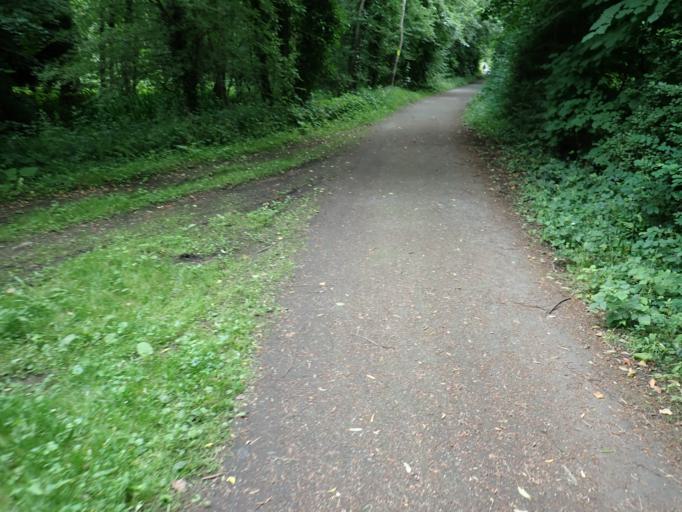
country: BE
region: Flanders
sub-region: Provincie Oost-Vlaanderen
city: Hamme
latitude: 51.1056
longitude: 4.1605
